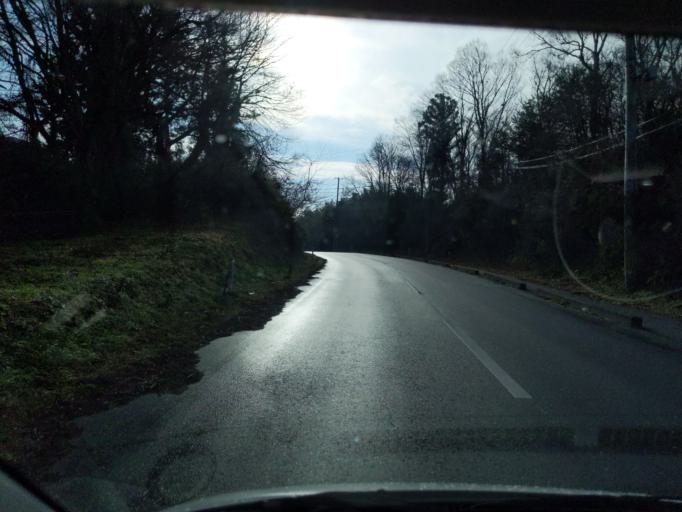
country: JP
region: Miyagi
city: Wakuya
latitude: 38.7057
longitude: 141.1592
